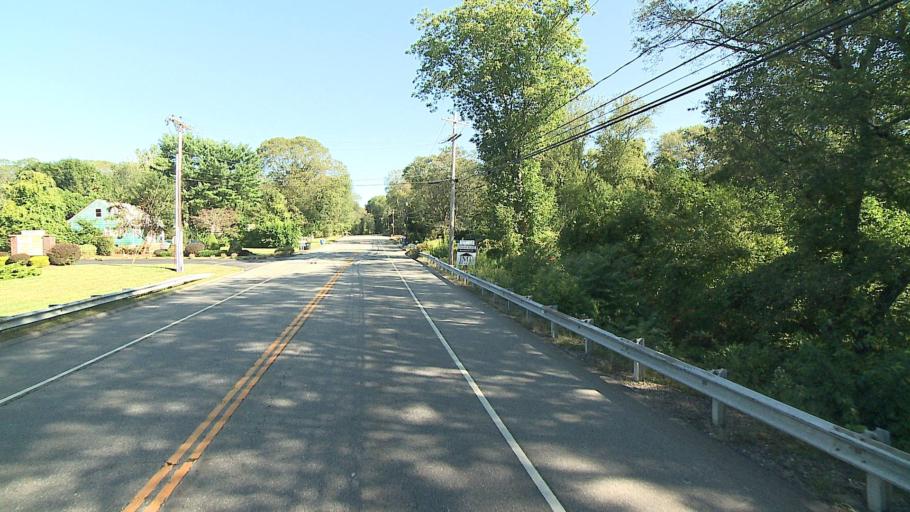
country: US
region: Connecticut
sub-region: New London County
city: Gales Ferry
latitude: 41.4116
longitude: -72.0734
